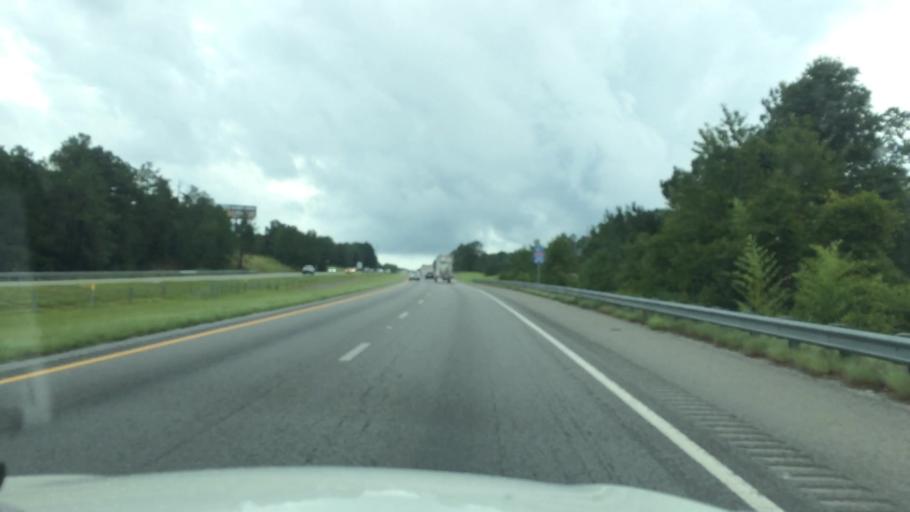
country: US
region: South Carolina
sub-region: Kershaw County
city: Lugoff
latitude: 34.1847
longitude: -80.6964
